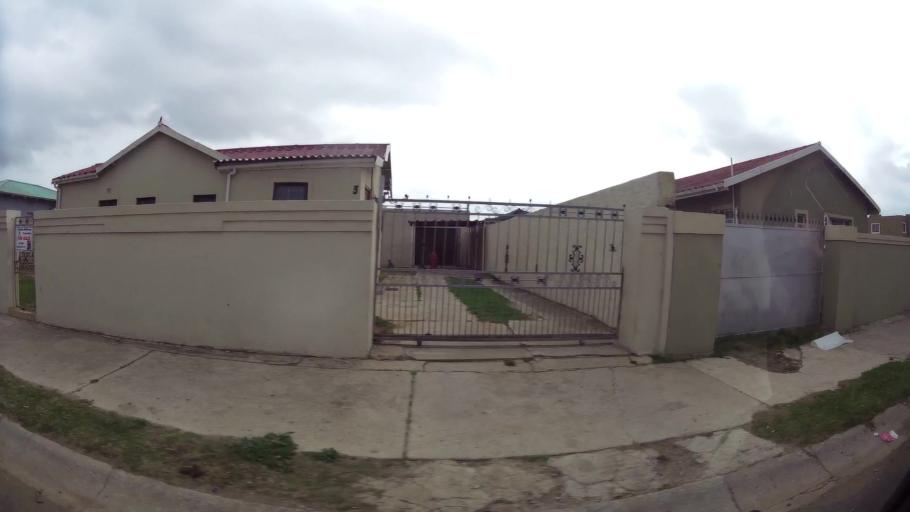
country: ZA
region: Eastern Cape
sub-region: Nelson Mandela Bay Metropolitan Municipality
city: Port Elizabeth
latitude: -33.8983
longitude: 25.5671
